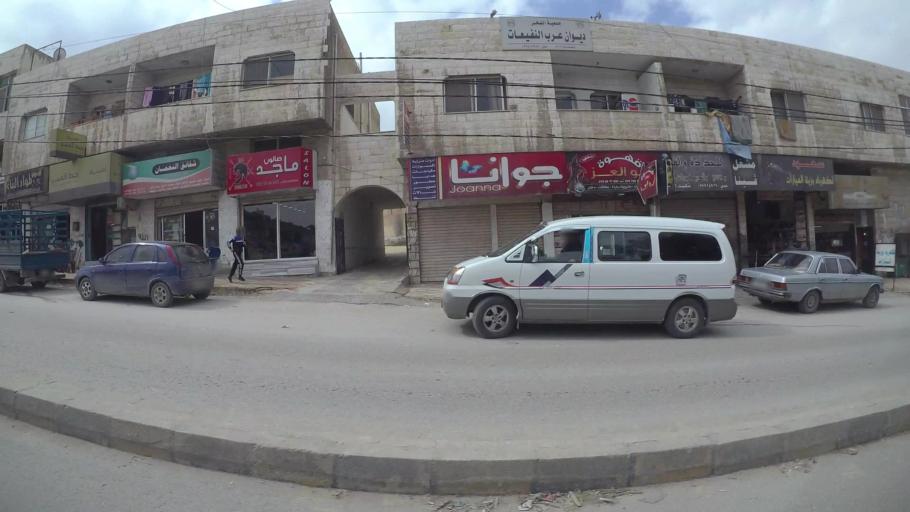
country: JO
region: Amman
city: Al Jubayhah
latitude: 32.0496
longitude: 35.8329
